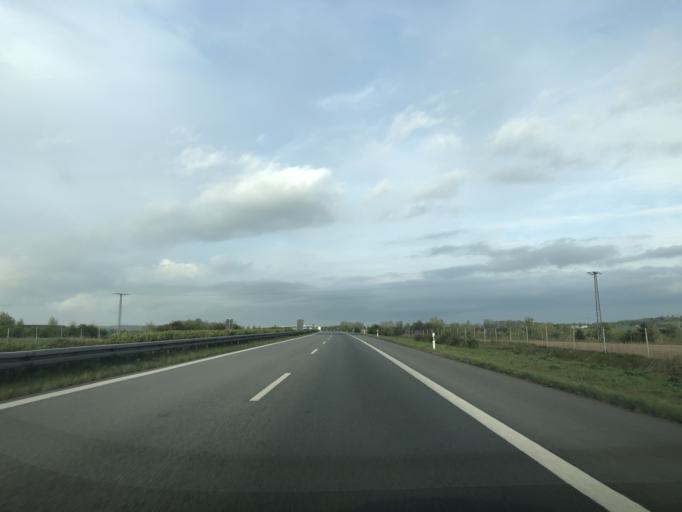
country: DE
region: Mecklenburg-Vorpommern
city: Bad Sulze
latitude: 54.0667
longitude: 12.7005
